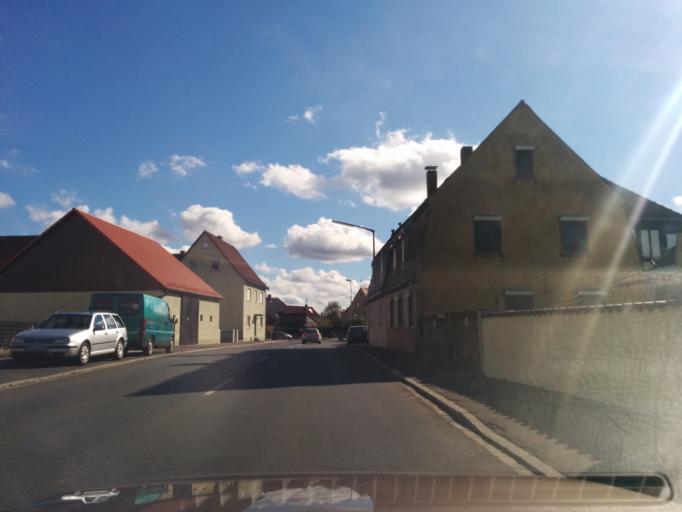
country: DE
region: Bavaria
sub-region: Regierungsbezirk Mittelfranken
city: Kalchreuth
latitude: 49.5572
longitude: 11.1266
